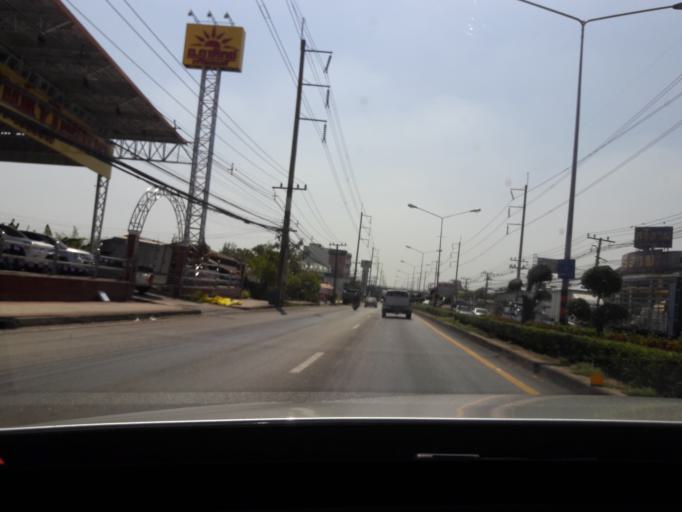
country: TH
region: Samut Sakhon
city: Krathum Baen
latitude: 13.6367
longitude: 100.2973
